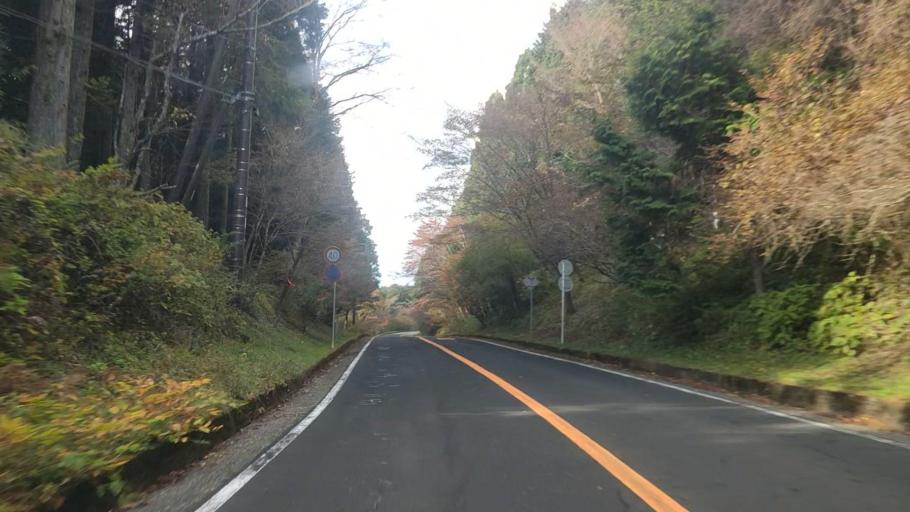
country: JP
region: Shizuoka
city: Fujinomiya
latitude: 35.3044
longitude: 138.6781
